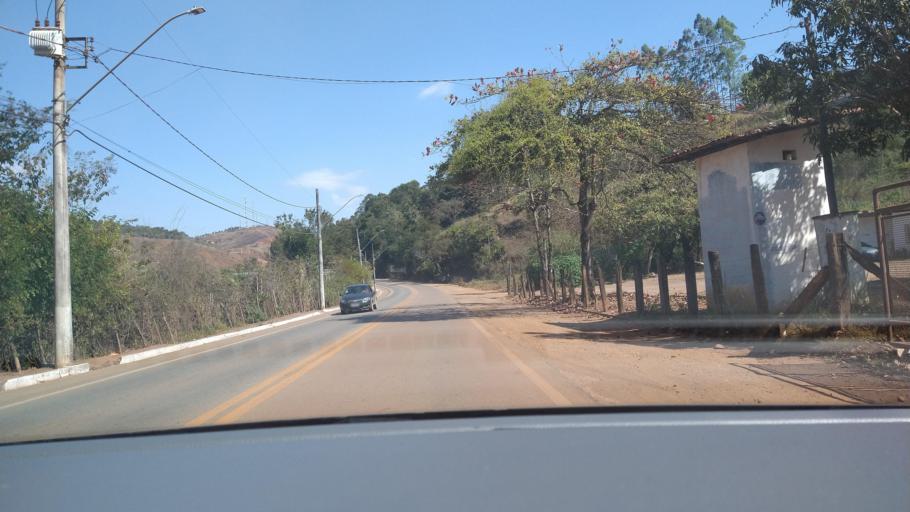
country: BR
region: Minas Gerais
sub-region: Rio Piracicaba
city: Rio Piracicaba
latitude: -19.9209
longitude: -43.1623
